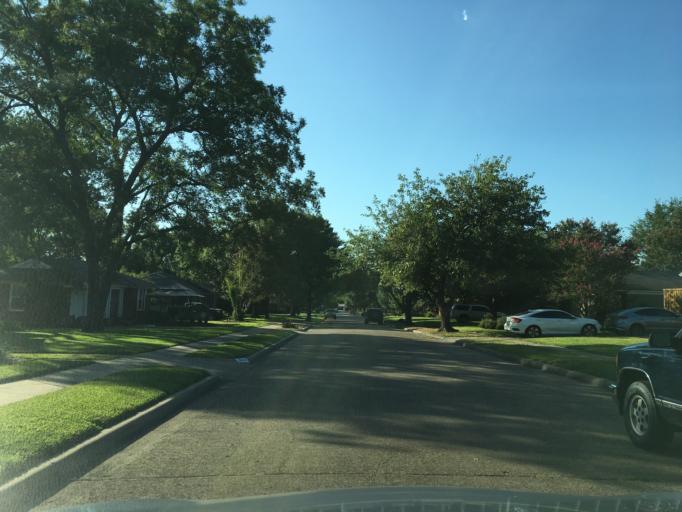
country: US
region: Texas
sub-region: Dallas County
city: Highland Park
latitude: 32.8524
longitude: -96.7128
